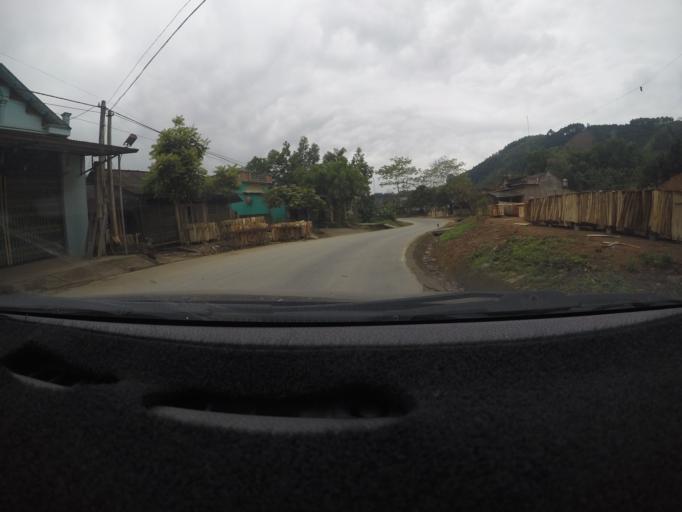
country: VN
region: Yen Bai
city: Co Phuc
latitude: 21.9242
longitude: 104.7984
